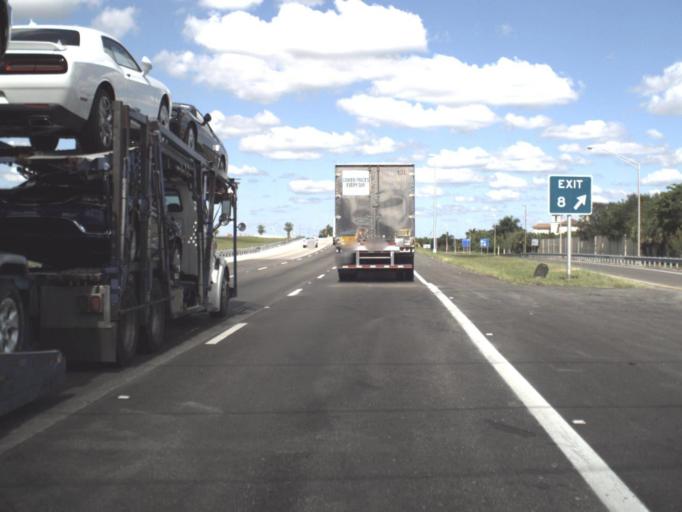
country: US
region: Florida
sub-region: Broward County
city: Tamarac
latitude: 26.2288
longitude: -80.2960
